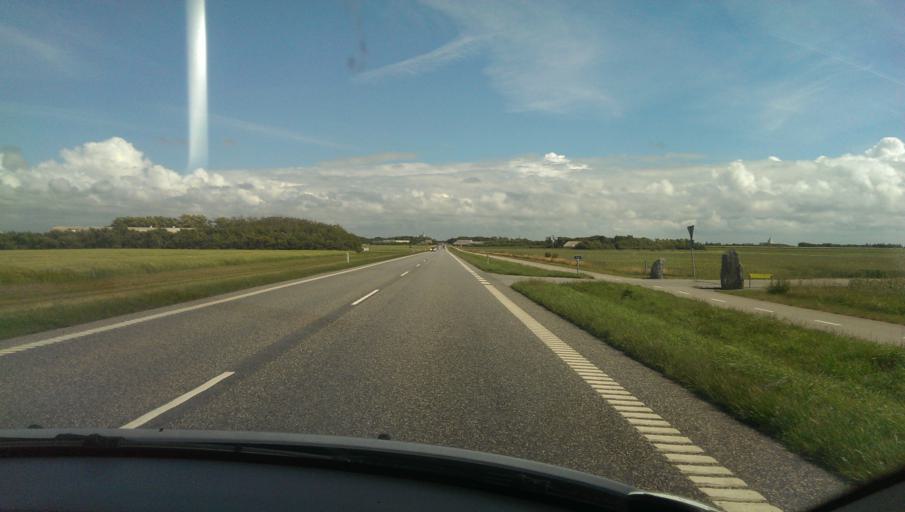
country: DK
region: Central Jutland
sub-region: Ringkobing-Skjern Kommune
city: Ringkobing
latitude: 56.1106
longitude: 8.1928
